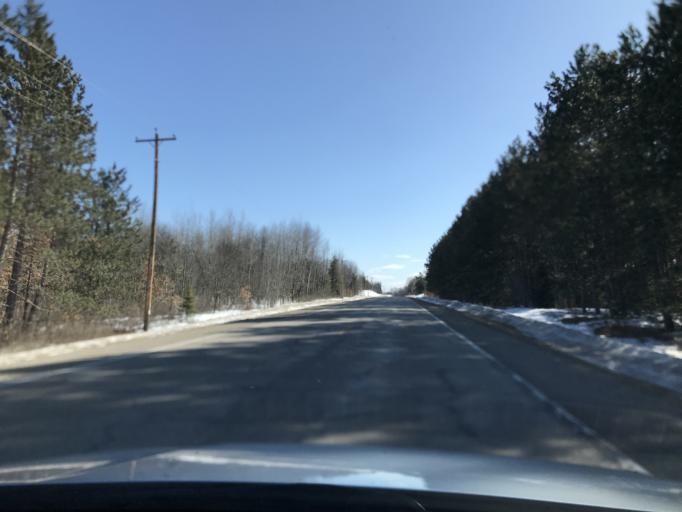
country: US
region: Wisconsin
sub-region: Marinette County
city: Niagara
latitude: 45.3475
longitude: -88.1014
